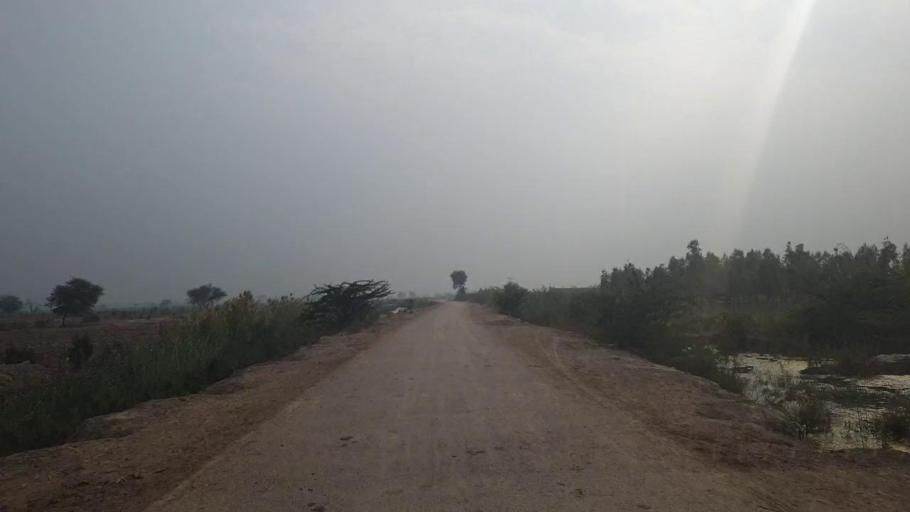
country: PK
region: Sindh
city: Tando Adam
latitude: 25.7885
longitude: 68.7086
